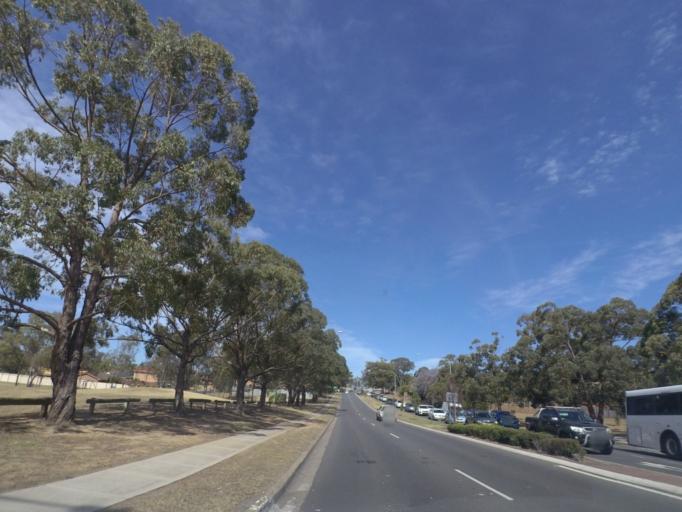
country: AU
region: New South Wales
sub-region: Campbelltown Municipality
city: Leumeah
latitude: -34.0301
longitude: 150.8275
